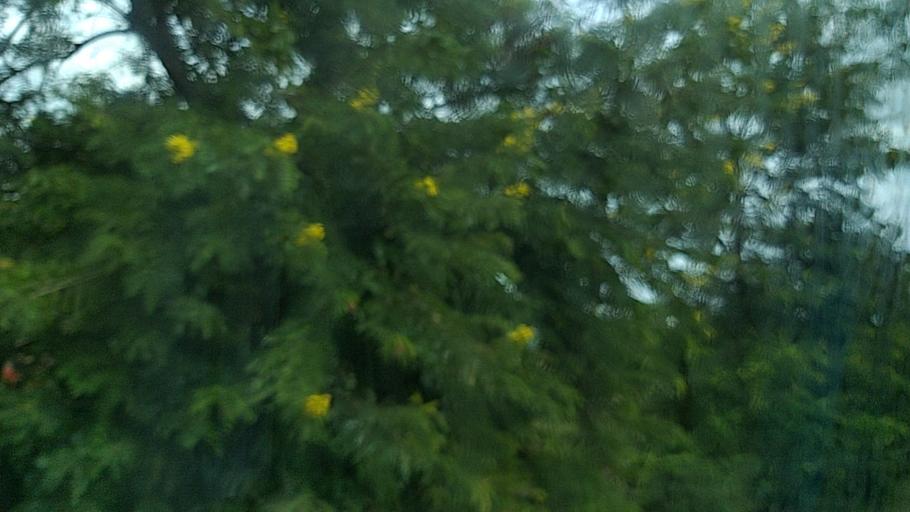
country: TH
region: Maha Sarakham
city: Maha Sarakham
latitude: 16.1515
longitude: 103.3812
